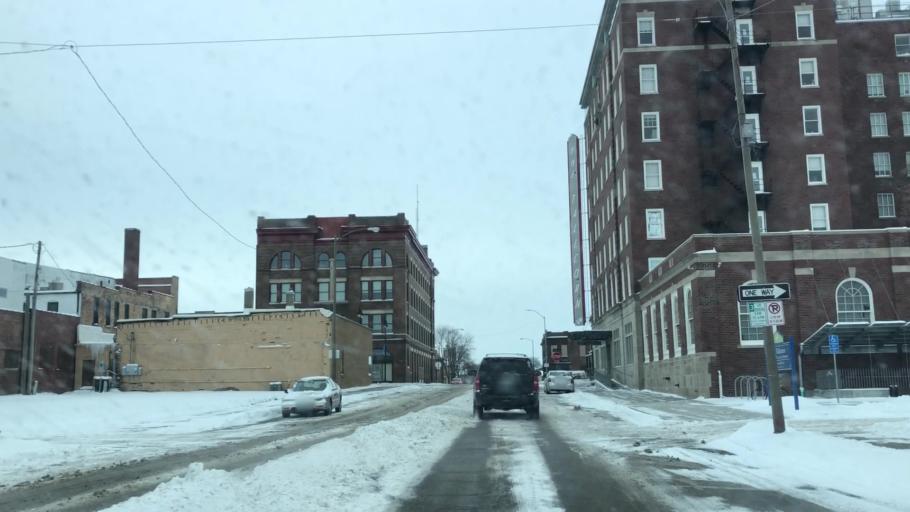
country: US
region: Iowa
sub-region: Marshall County
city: Marshalltown
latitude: 42.0499
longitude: -92.9097
